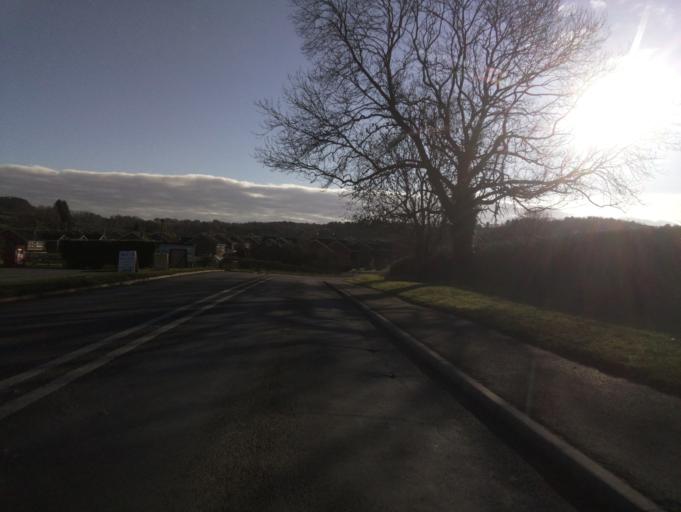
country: GB
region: England
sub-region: Staffordshire
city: Uttoxeter
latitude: 52.8570
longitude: -1.7699
